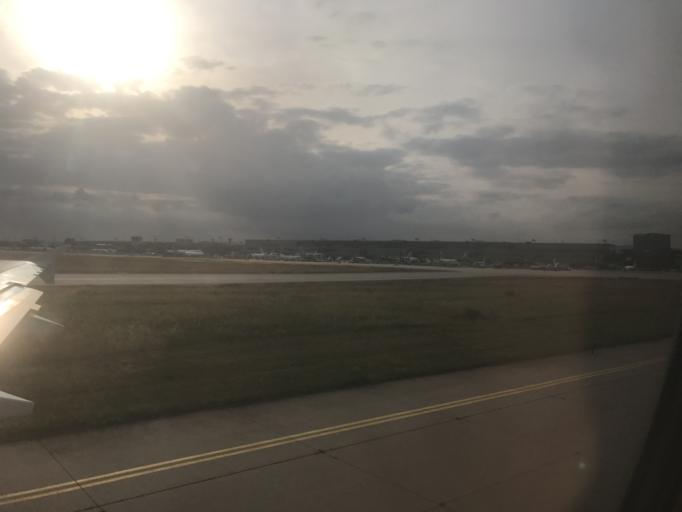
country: DE
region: Hesse
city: Niederrad
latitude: 50.0463
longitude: 8.5962
